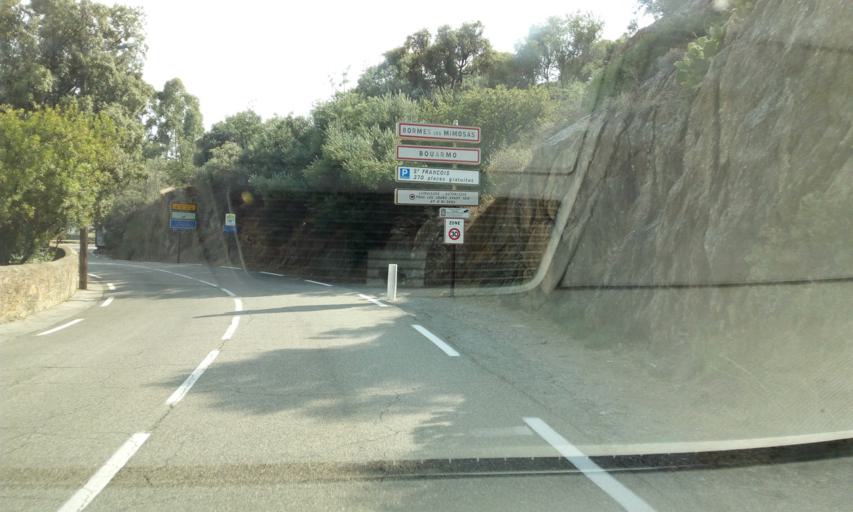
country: FR
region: Provence-Alpes-Cote d'Azur
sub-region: Departement du Var
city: Bormes-les-Mimosas
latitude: 43.1534
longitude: 6.3452
